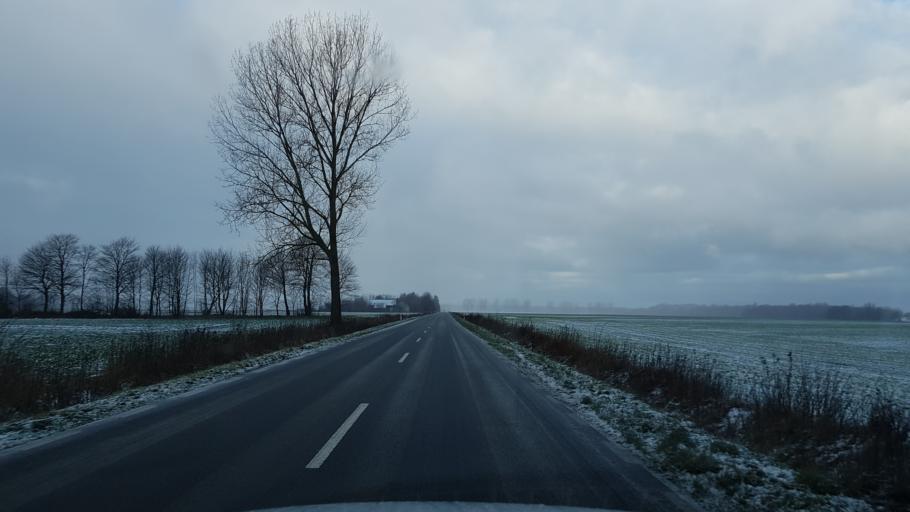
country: PL
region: West Pomeranian Voivodeship
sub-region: Powiat gryficki
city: Karnice
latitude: 54.0152
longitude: 15.0796
